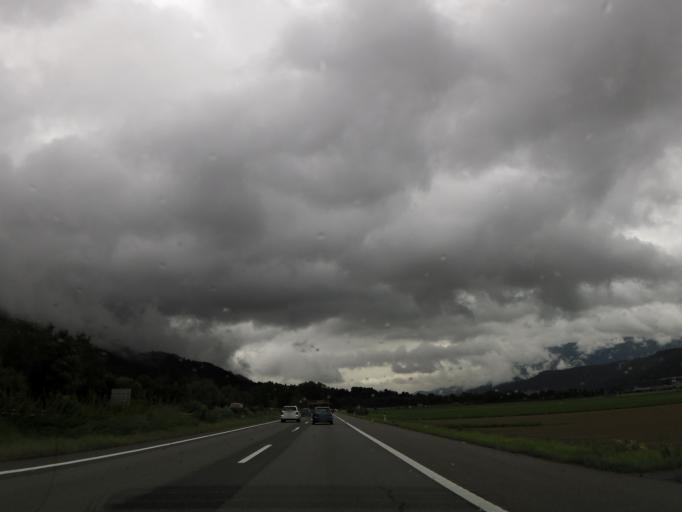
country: AT
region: Tyrol
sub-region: Politischer Bezirk Innsbruck Land
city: Gotzens
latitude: 47.2638
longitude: 11.3078
